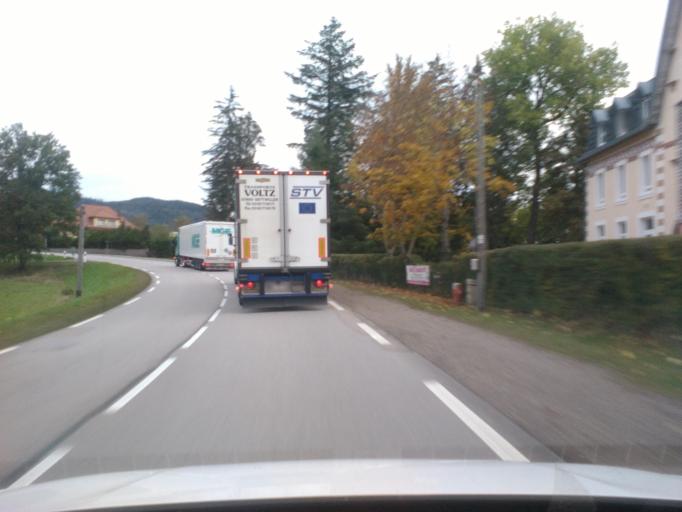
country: FR
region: Lorraine
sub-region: Departement des Vosges
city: Ban-de-Laveline
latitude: 48.3425
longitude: 7.1075
